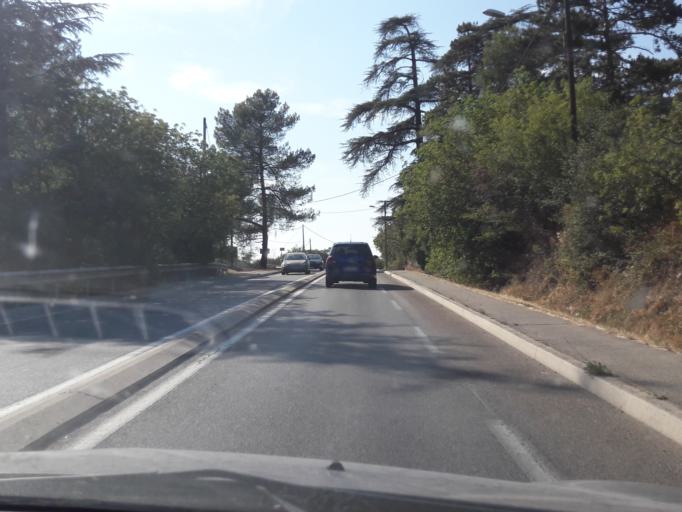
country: FR
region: Provence-Alpes-Cote d'Azur
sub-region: Departement des Bouches-du-Rhone
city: Bouc-Bel-Air
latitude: 43.4772
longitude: 5.4280
